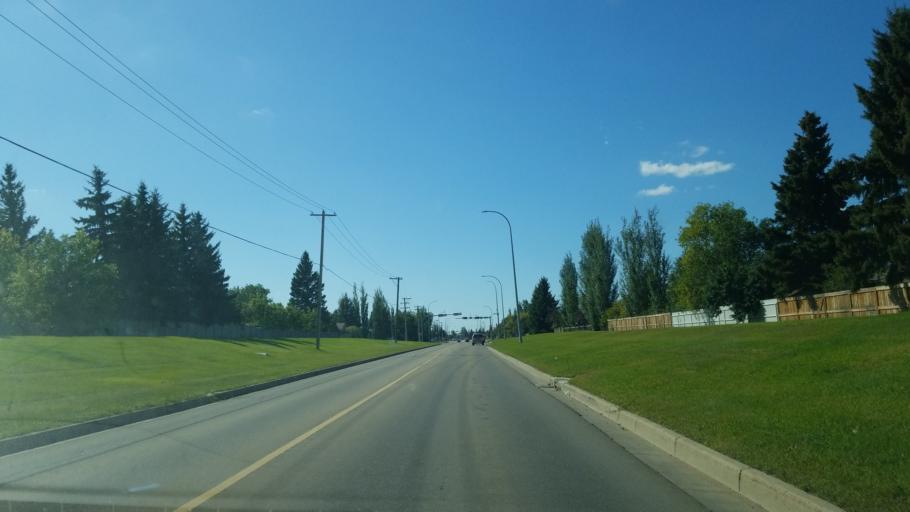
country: CA
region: Saskatchewan
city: Lloydminster
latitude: 53.2707
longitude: -110.0216
